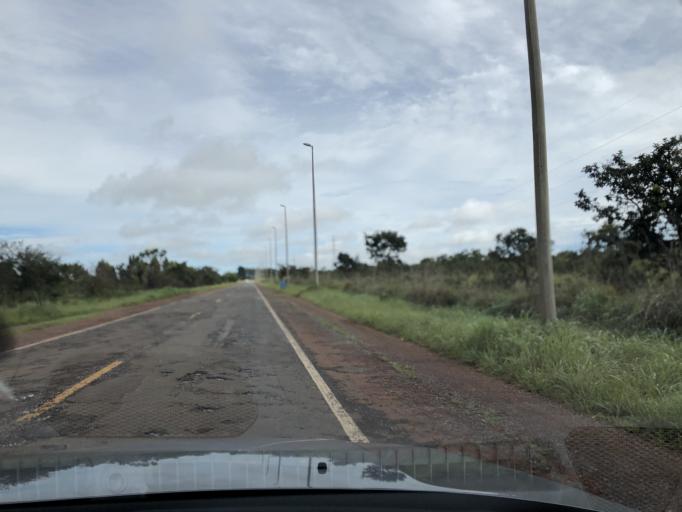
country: BR
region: Federal District
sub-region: Brasilia
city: Brasilia
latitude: -15.6889
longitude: -48.0890
